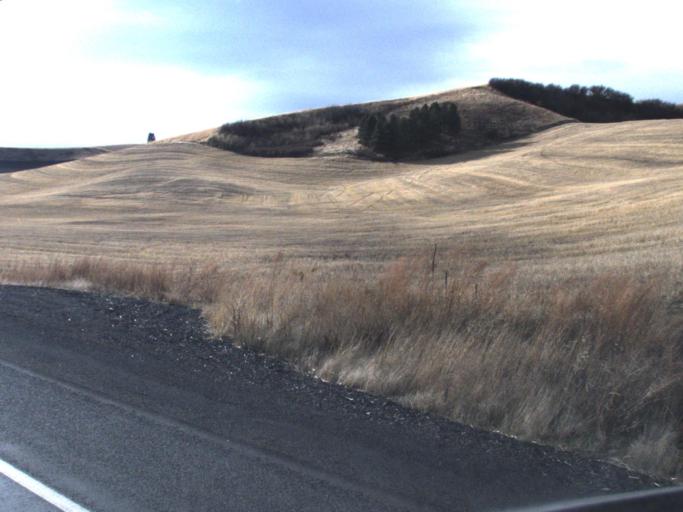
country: US
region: Washington
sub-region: Whitman County
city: Colfax
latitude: 46.8808
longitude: -117.3943
